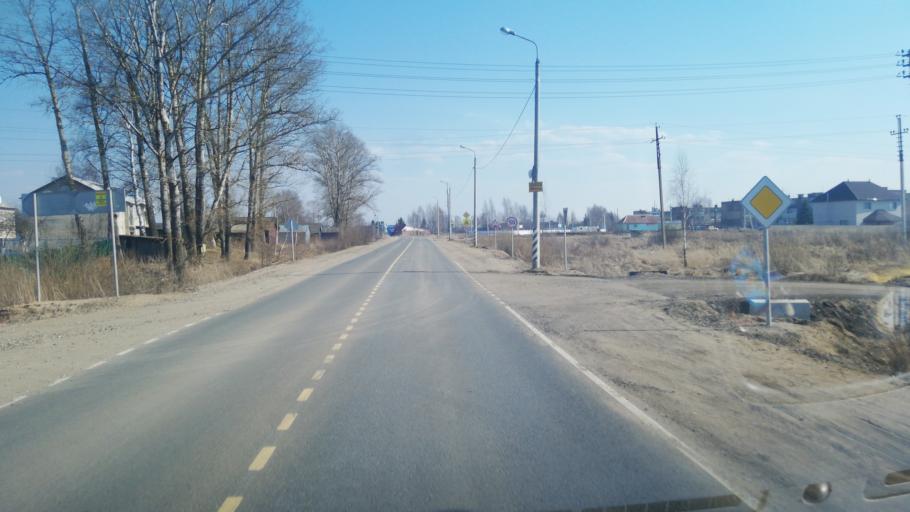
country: RU
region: Jaroslavl
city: Semibratovo
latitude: 57.2336
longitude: 39.4921
